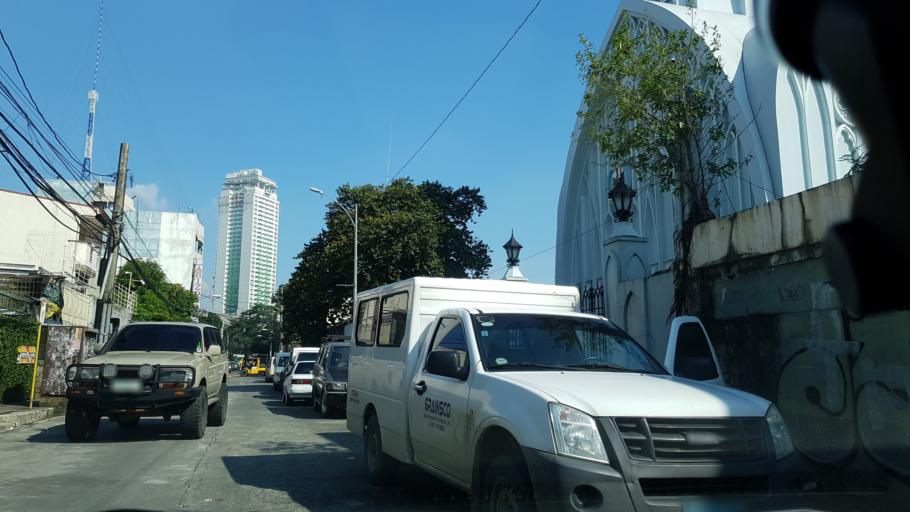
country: PH
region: Metro Manila
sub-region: Quezon City
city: Quezon City
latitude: 14.6232
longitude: 121.0466
